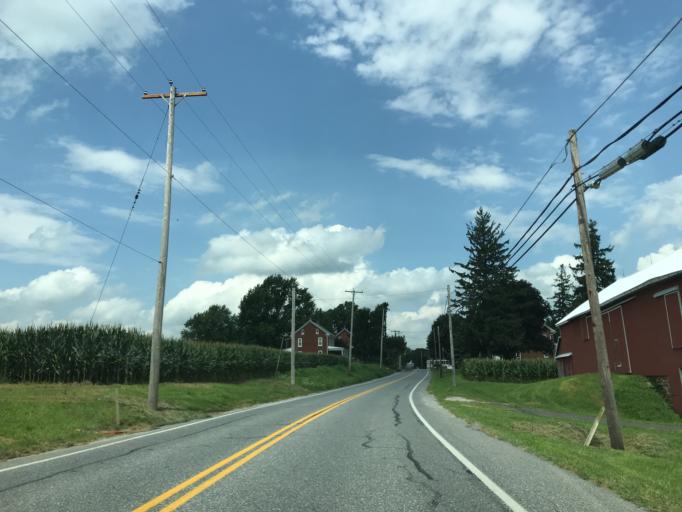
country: US
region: Pennsylvania
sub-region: York County
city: Red Lion
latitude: 39.8459
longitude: -76.6208
